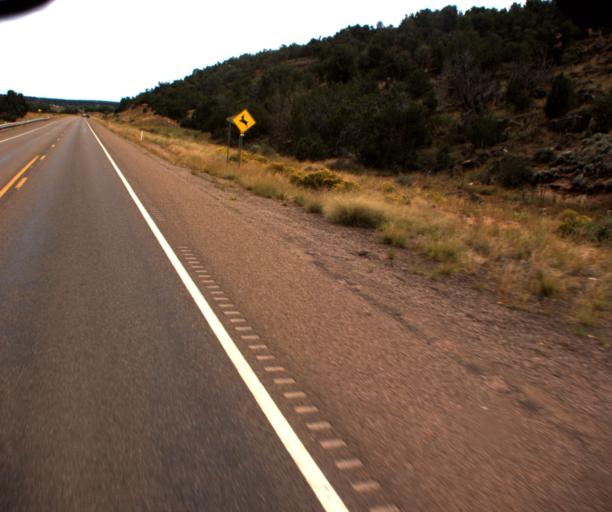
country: US
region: Arizona
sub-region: Navajo County
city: Taylor
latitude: 34.3979
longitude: -110.0685
